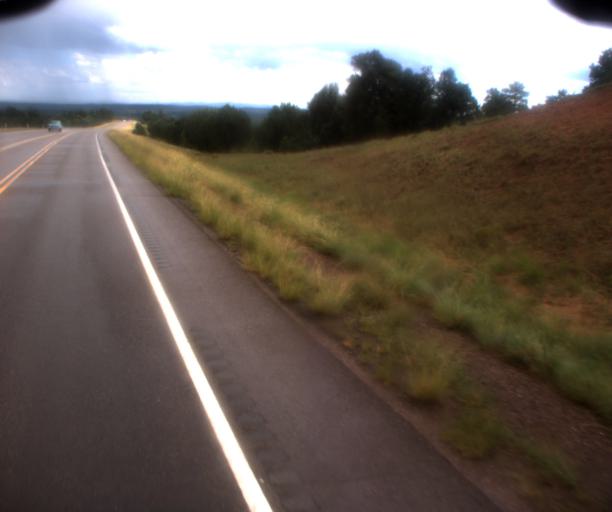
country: US
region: Arizona
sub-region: Navajo County
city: Heber-Overgaard
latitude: 34.3670
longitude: -110.3652
